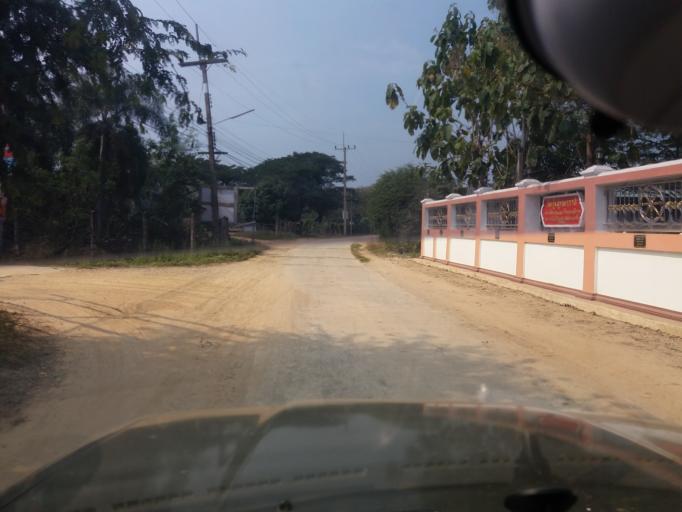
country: TH
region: Sing Buri
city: Bang Racham
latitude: 14.8953
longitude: 100.2045
